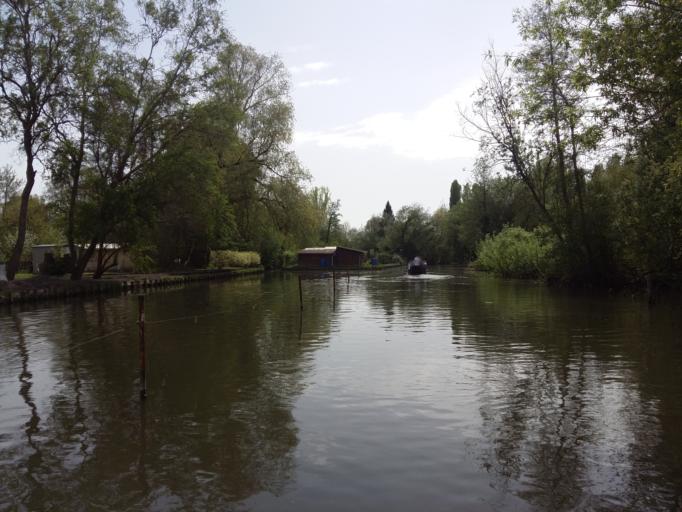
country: FR
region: Picardie
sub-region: Departement de la Somme
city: Rivery
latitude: 49.8961
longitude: 2.3276
